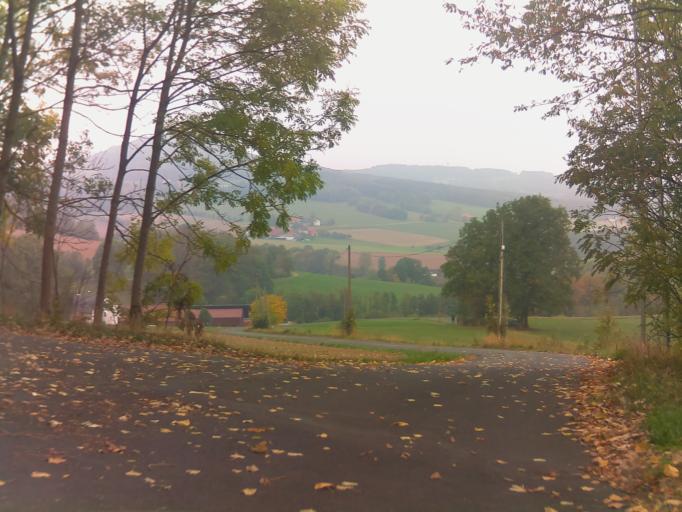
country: DE
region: Hesse
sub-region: Regierungsbezirk Kassel
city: Poppenhausen
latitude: 50.4992
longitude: 9.8640
